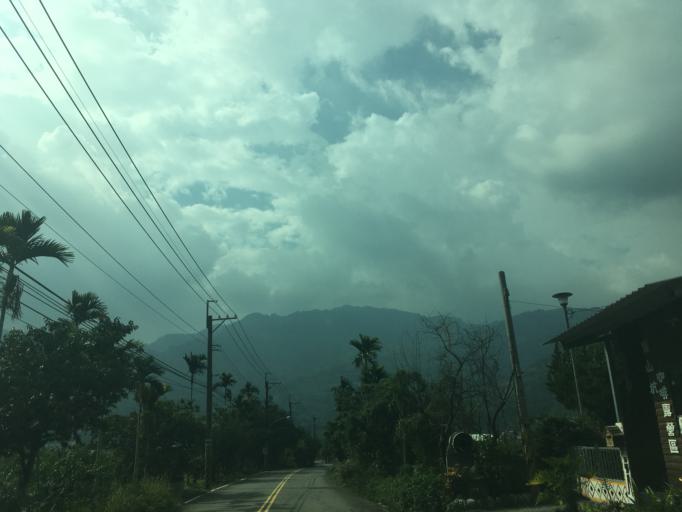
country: TW
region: Taiwan
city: Fengyuan
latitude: 24.3362
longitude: 120.9346
